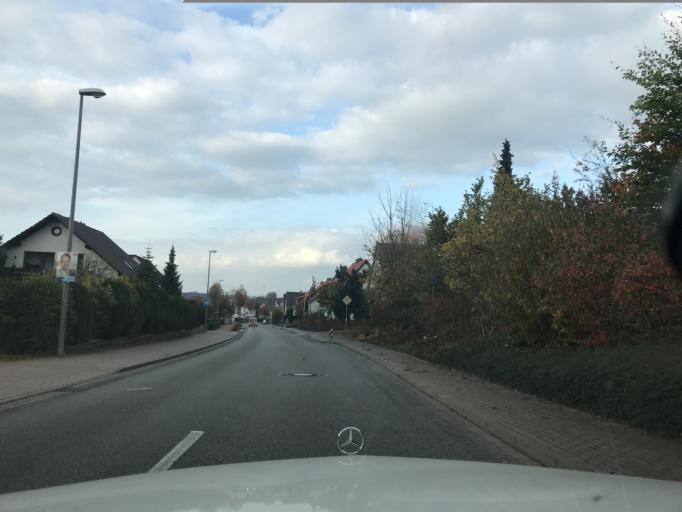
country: DE
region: Hesse
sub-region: Regierungsbezirk Kassel
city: Breuna
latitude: 51.4098
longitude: 9.1830
